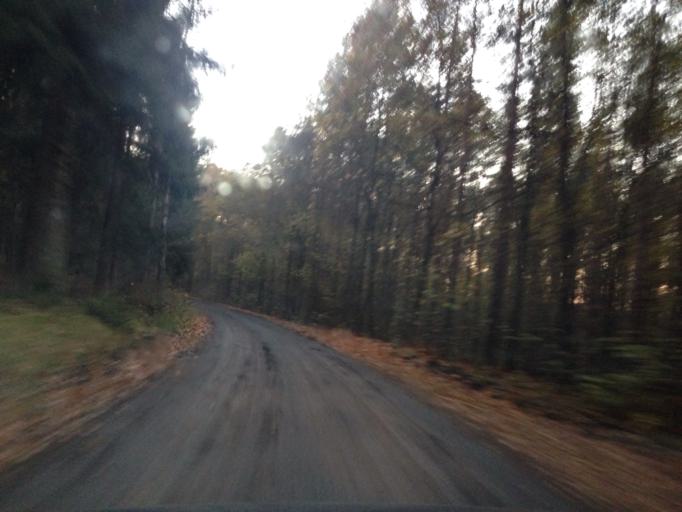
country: PL
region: Kujawsko-Pomorskie
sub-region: Powiat brodnicki
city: Gorzno
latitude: 53.2248
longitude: 19.6959
